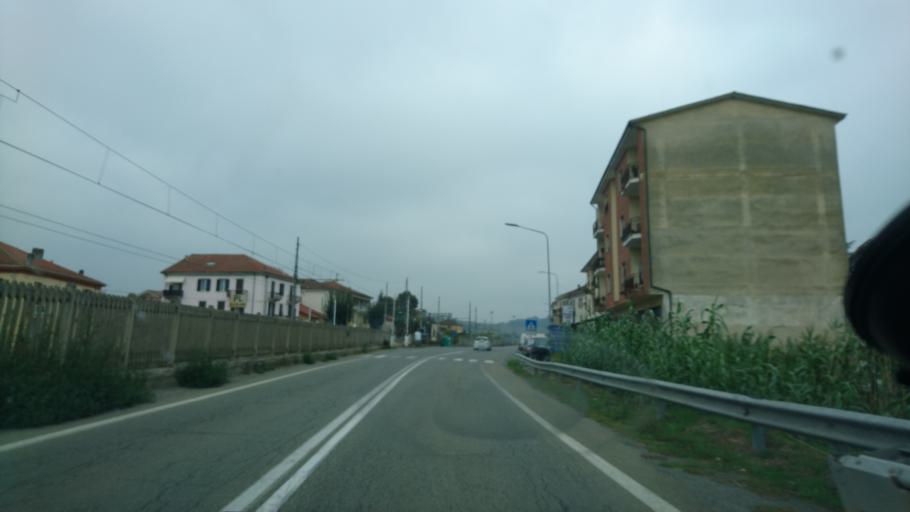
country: IT
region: Piedmont
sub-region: Provincia di Alessandria
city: Bistagno
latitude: 44.6587
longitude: 8.3693
